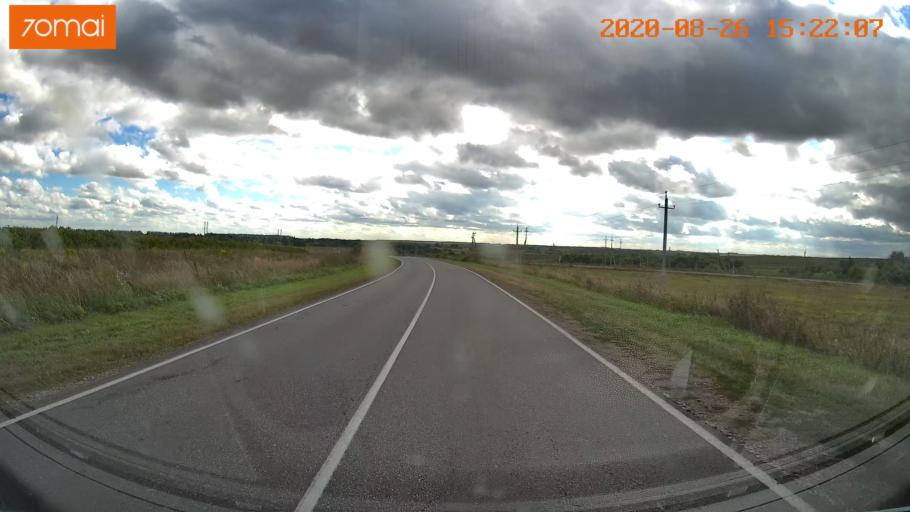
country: RU
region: Tula
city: Severo-Zadonsk
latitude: 54.1360
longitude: 38.4555
